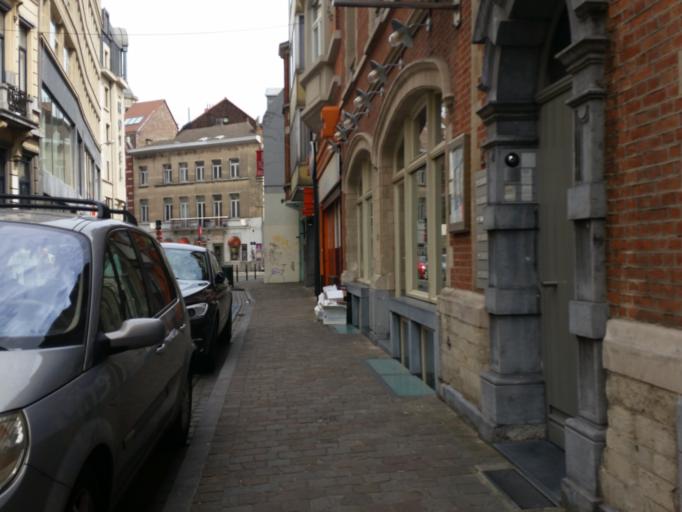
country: BE
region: Brussels Capital
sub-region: Bruxelles-Capitale
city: Brussels
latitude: 50.8514
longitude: 4.3498
